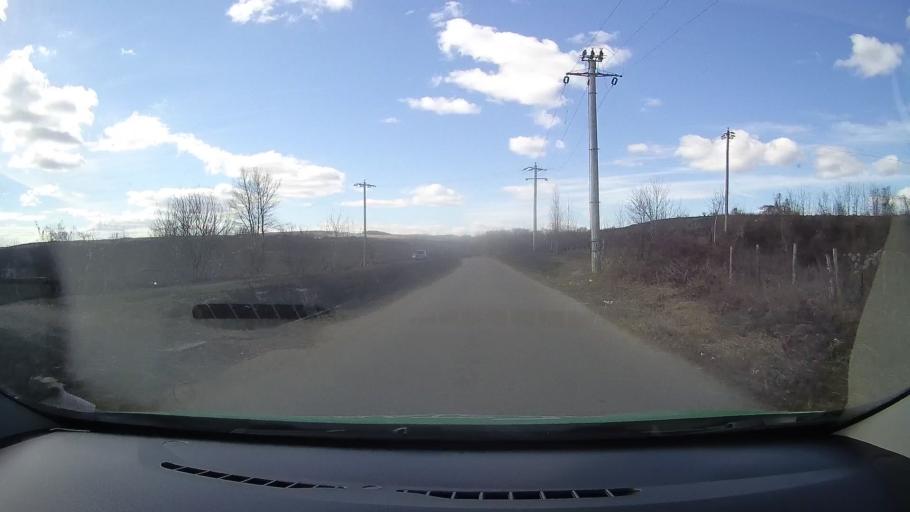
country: RO
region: Dambovita
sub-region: Comuna Doicesti
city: Doicesti
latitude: 44.9959
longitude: 25.3894
